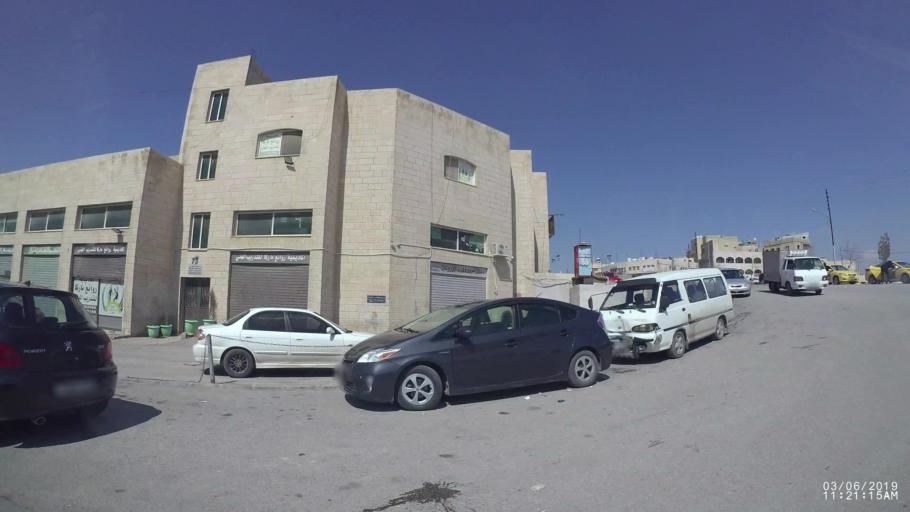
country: JO
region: Amman
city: Amman
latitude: 31.9800
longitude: 35.9982
